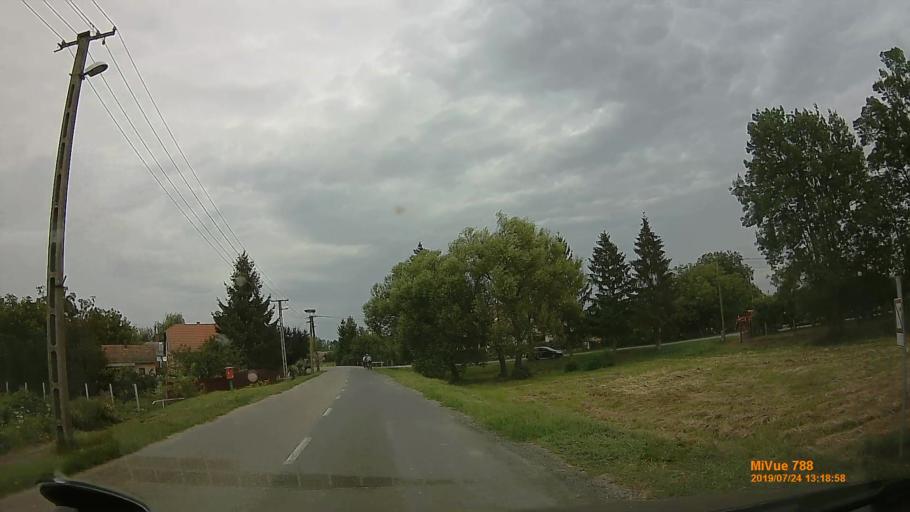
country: HU
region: Szabolcs-Szatmar-Bereg
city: Vasarosnameny
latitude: 48.1941
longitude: 22.4070
